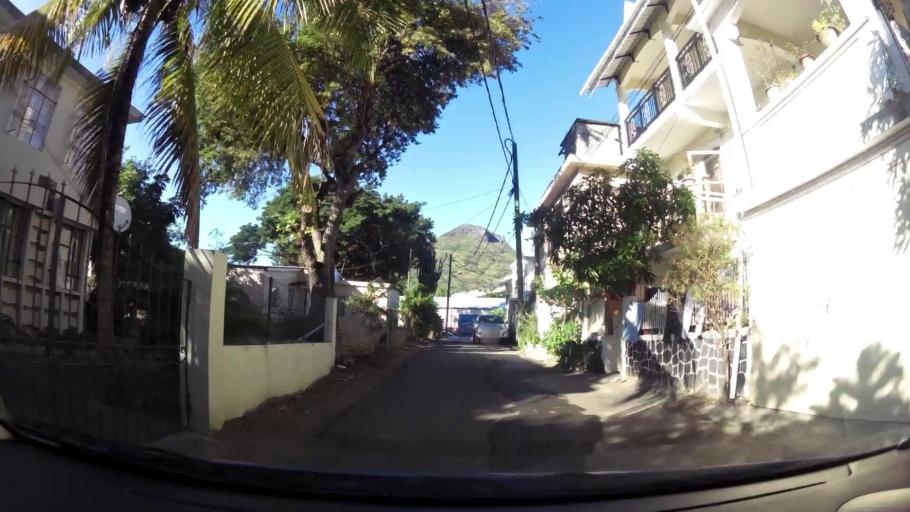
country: MU
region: Black River
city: Tamarin
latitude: -20.3289
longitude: 57.3788
